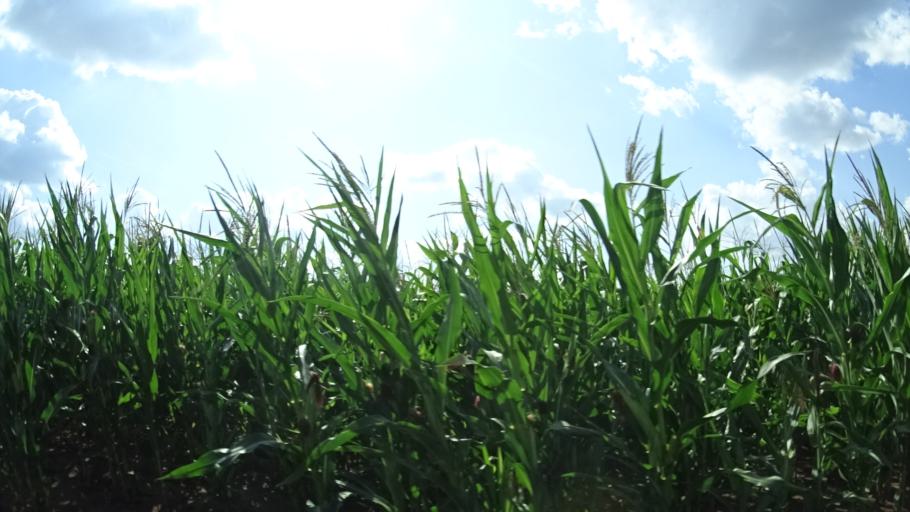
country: DE
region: Bavaria
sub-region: Regierungsbezirk Unterfranken
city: Trappstadt
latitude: 50.2879
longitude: 10.5853
